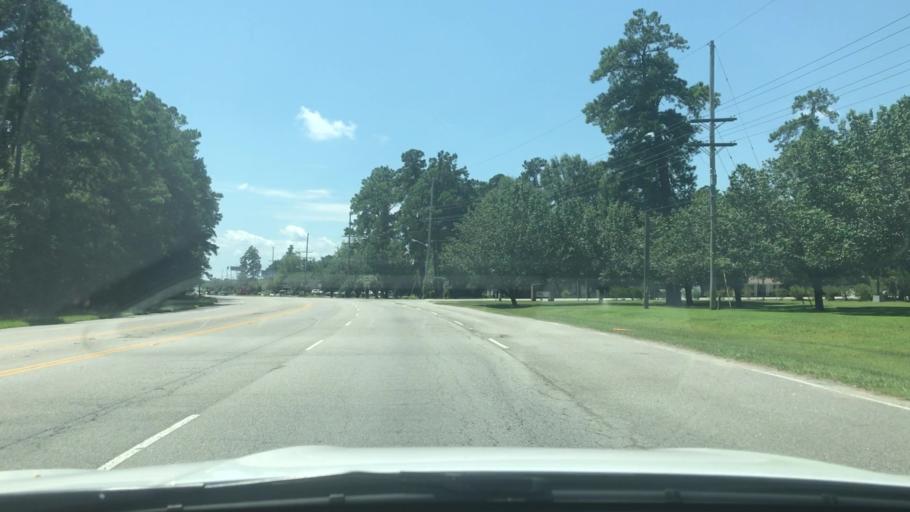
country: US
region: South Carolina
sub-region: Horry County
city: Conway
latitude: 33.8728
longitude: -79.0512
